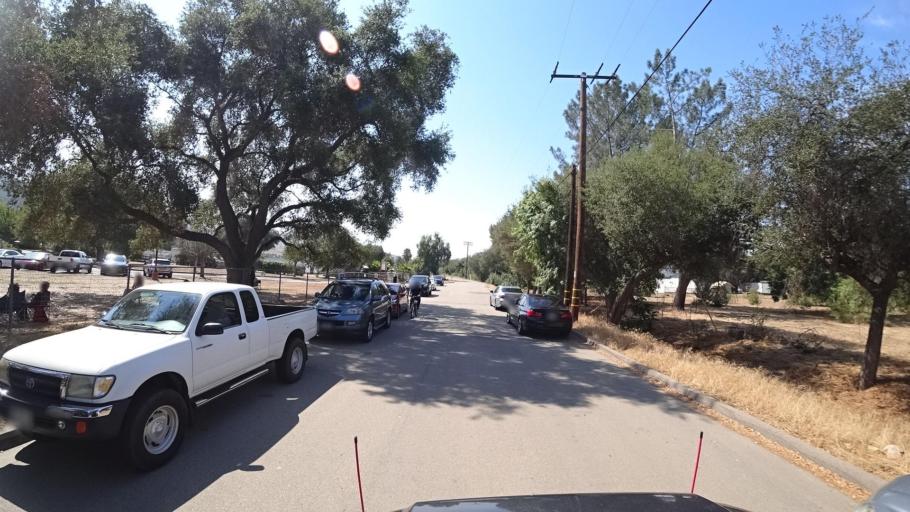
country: US
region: California
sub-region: San Diego County
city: Hidden Meadows
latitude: 33.1956
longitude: -117.1522
